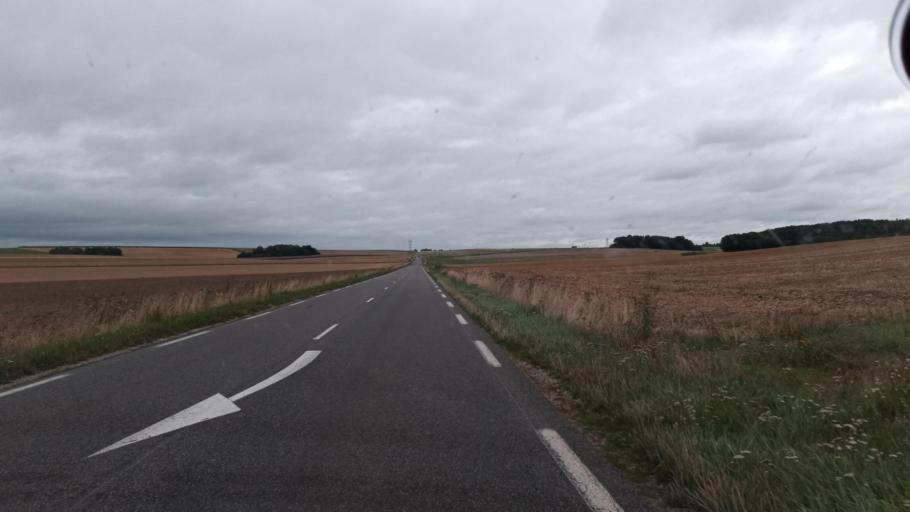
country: FR
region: Ile-de-France
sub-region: Departement de Seine-et-Marne
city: Voulx
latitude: 48.3161
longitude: 2.9493
